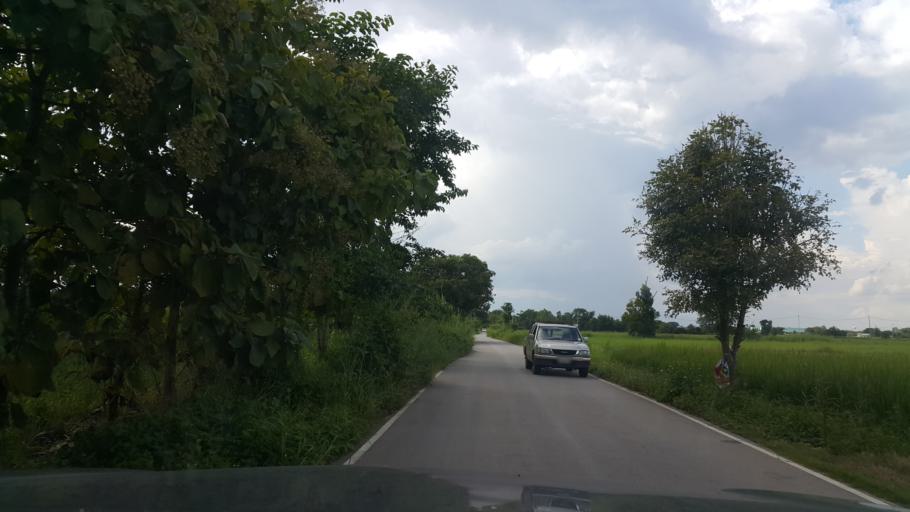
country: TH
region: Chiang Mai
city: San Kamphaeng
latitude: 18.7097
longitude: 99.1583
